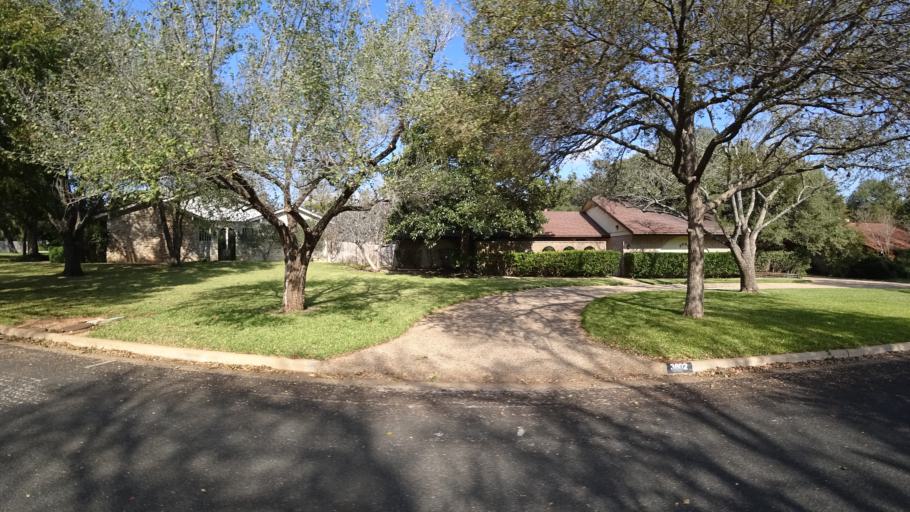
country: US
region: Texas
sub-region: Travis County
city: Shady Hollow
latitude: 30.1674
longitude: -97.8638
